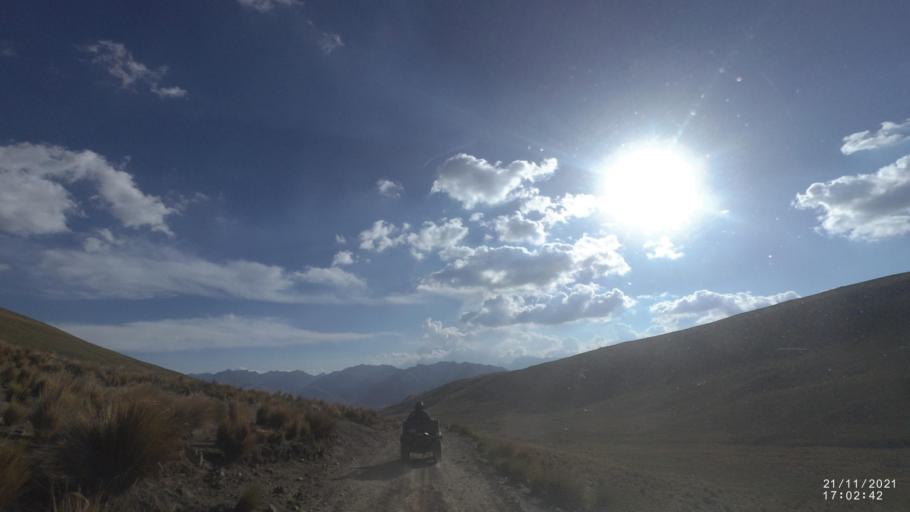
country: BO
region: Cochabamba
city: Cochabamba
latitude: -17.1171
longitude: -66.2553
